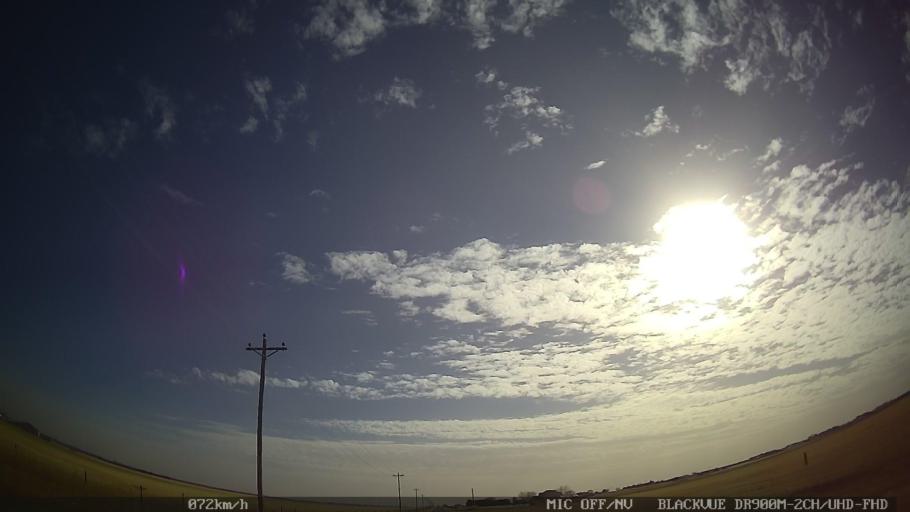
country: US
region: New Mexico
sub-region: Curry County
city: Texico
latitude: 34.4260
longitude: -103.0906
